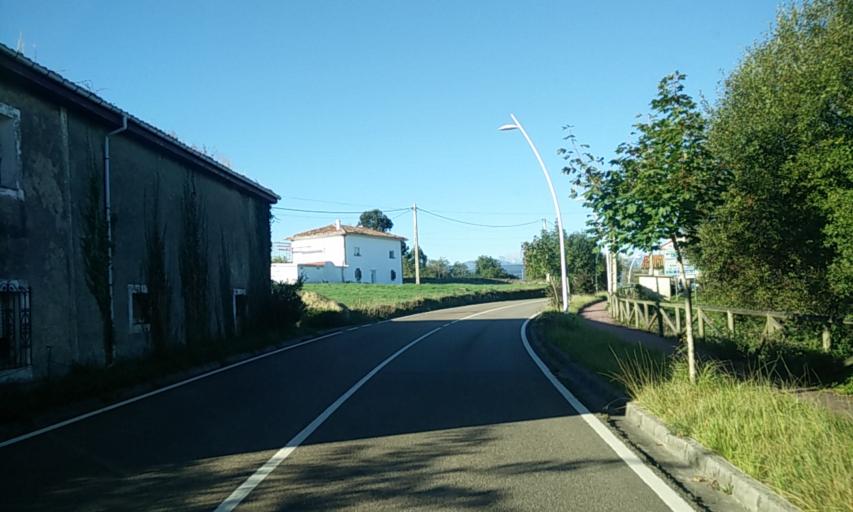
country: ES
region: Cantabria
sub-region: Provincia de Cantabria
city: San Vicente de la Barquera
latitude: 43.3746
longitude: -4.3663
